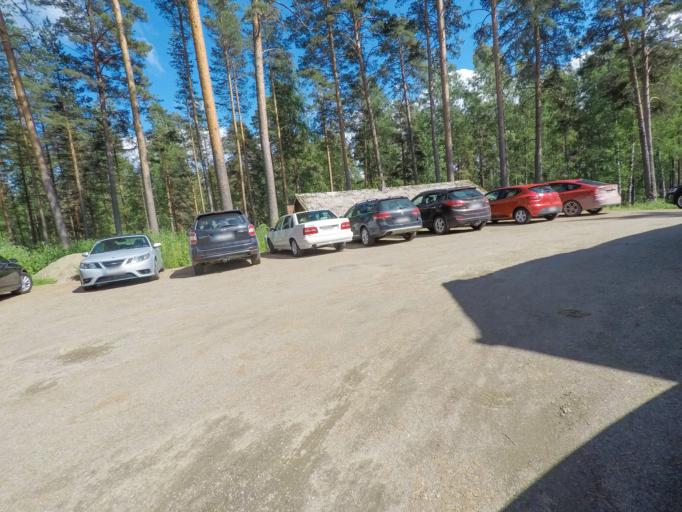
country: FI
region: Southern Savonia
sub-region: Savonlinna
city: Punkaharju
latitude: 61.8018
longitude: 29.3071
